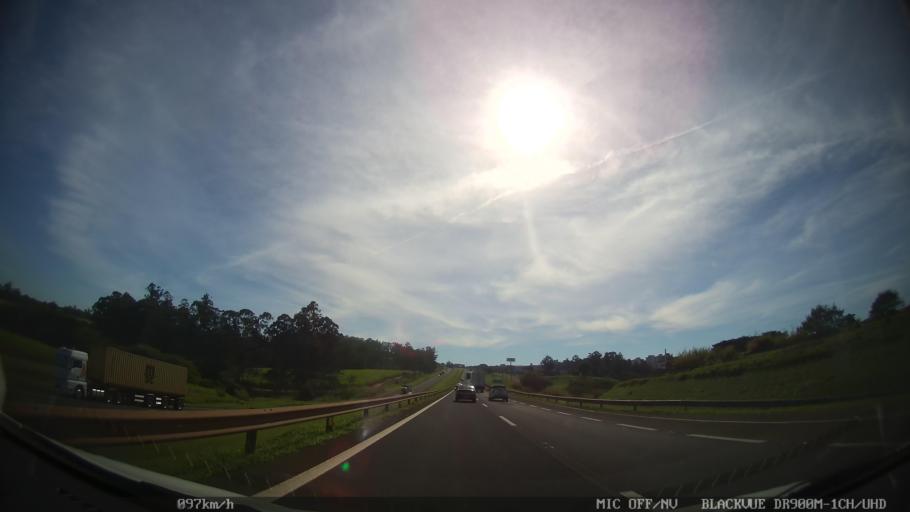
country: BR
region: Sao Paulo
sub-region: Araras
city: Araras
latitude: -22.3421
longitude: -47.3924
